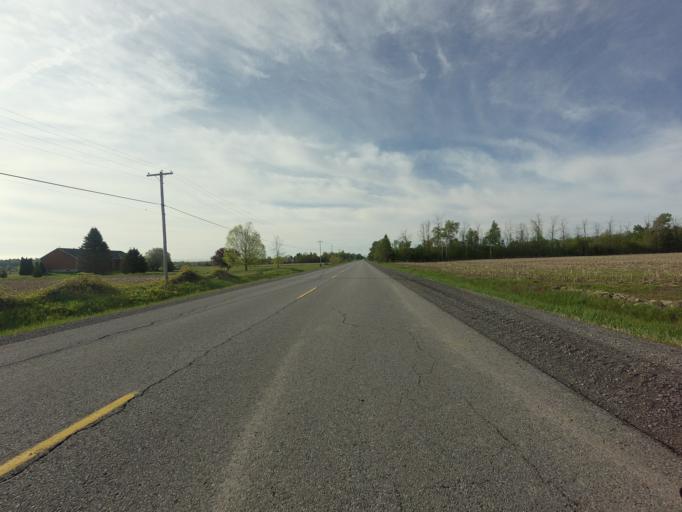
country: CA
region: Ontario
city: Ottawa
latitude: 45.2760
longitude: -75.4408
